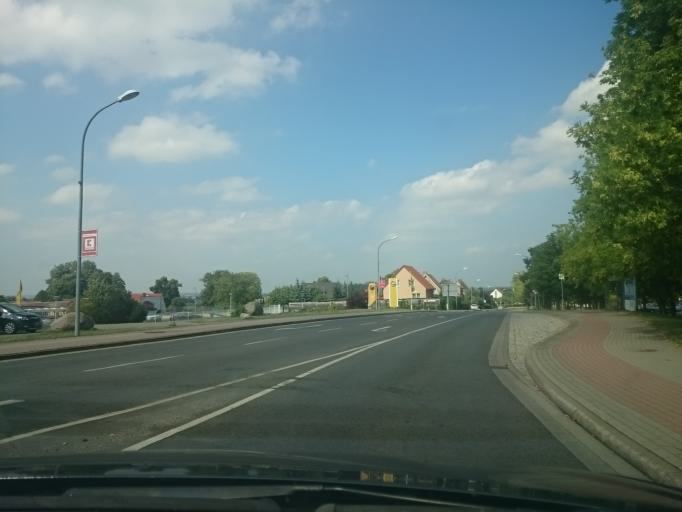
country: DE
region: Mecklenburg-Vorpommern
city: Pasewalk
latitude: 53.5032
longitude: 14.0031
